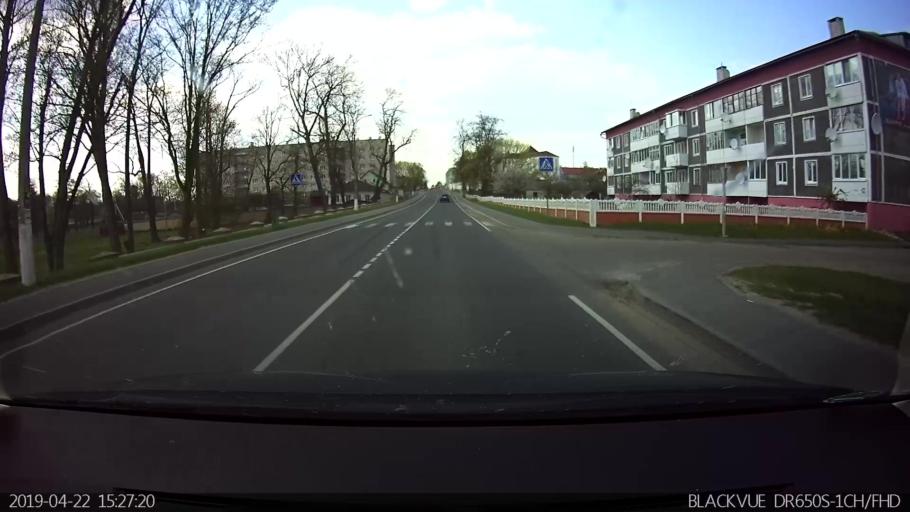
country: BY
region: Brest
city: Vysokaye
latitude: 52.3701
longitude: 23.3728
